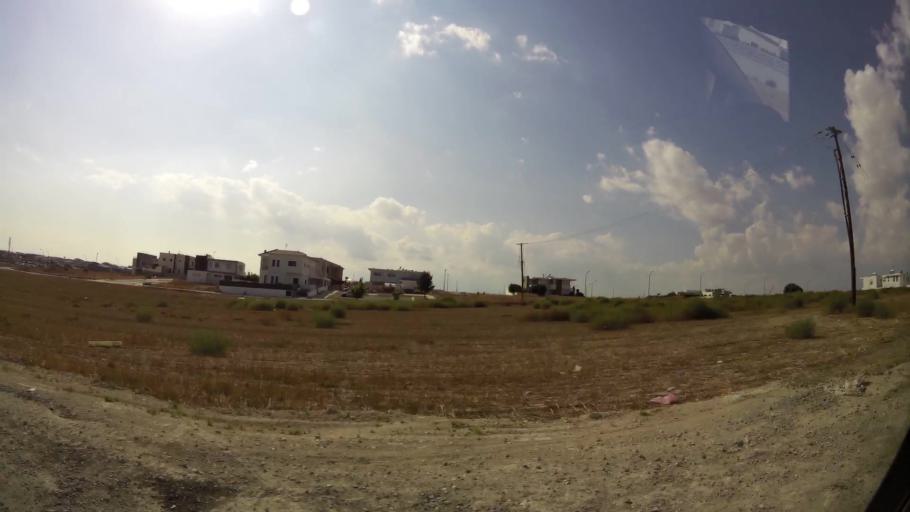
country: CY
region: Larnaka
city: Dhromolaxia
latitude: 34.9064
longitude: 33.5815
